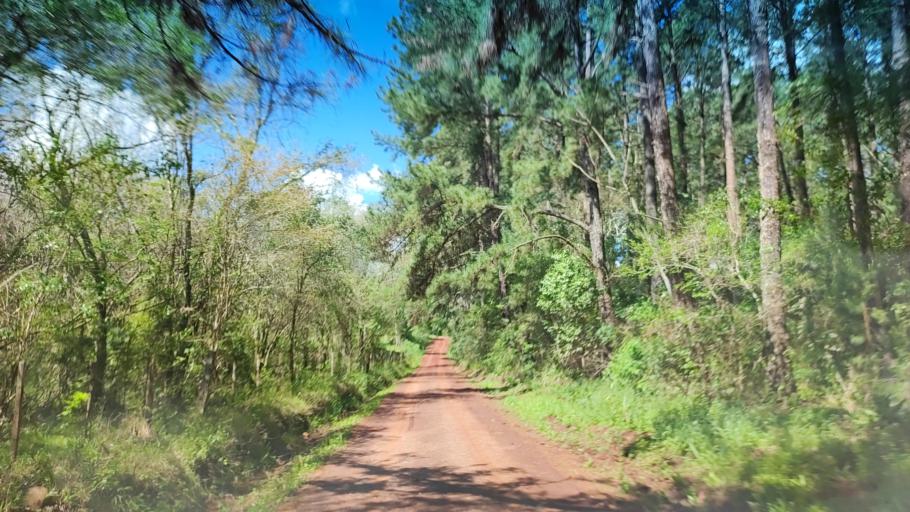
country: AR
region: Misiones
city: Ruiz de Montoya
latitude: -26.9529
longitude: -55.0311
